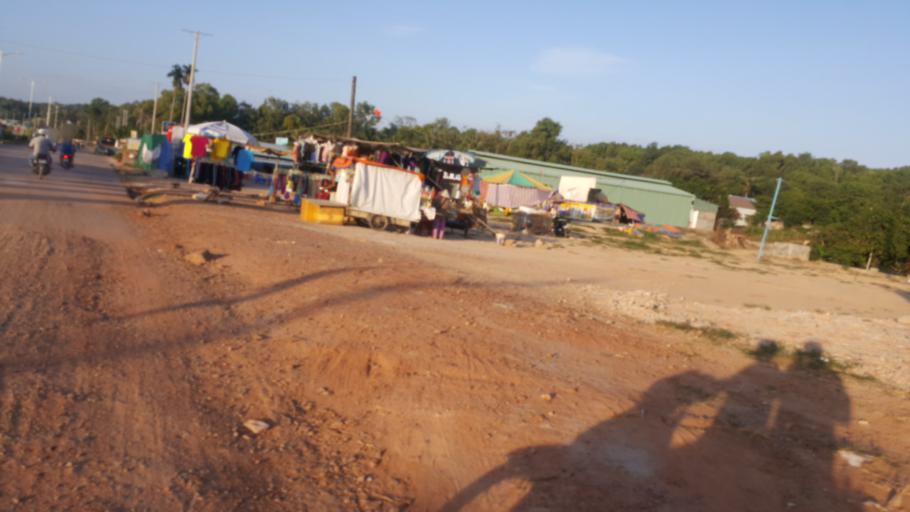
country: VN
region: Kien Giang
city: Duong GJong
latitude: 10.0308
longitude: 104.0172
